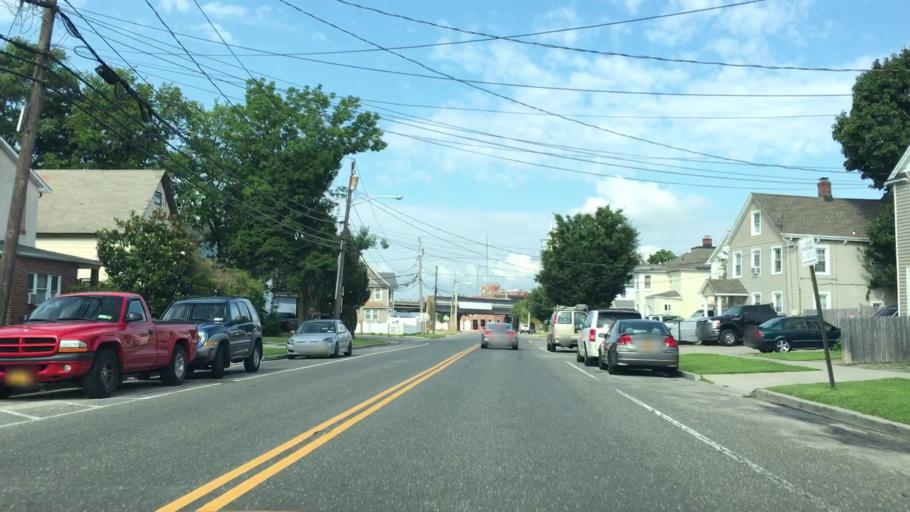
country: US
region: New York
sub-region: Nassau County
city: Hicksville
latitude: 40.7682
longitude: -73.5192
